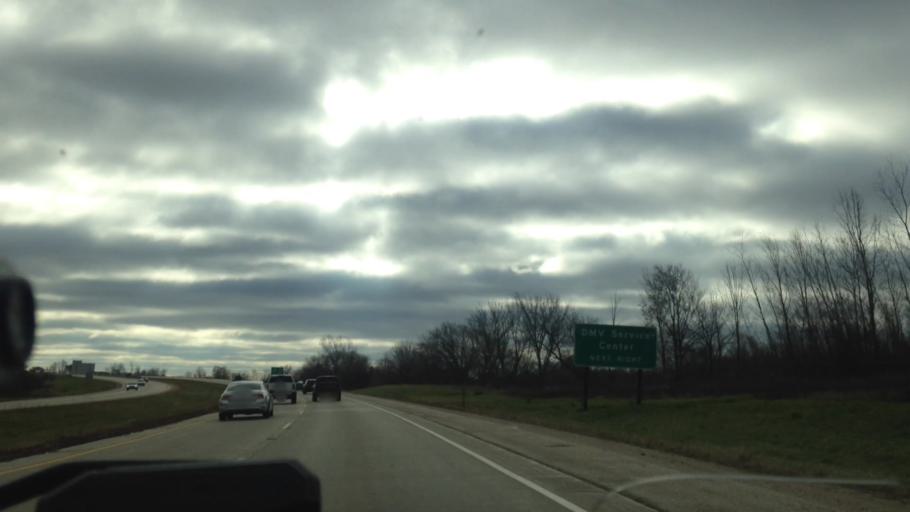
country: US
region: Wisconsin
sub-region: Washington County
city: West Bend
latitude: 43.4116
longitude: -88.2055
